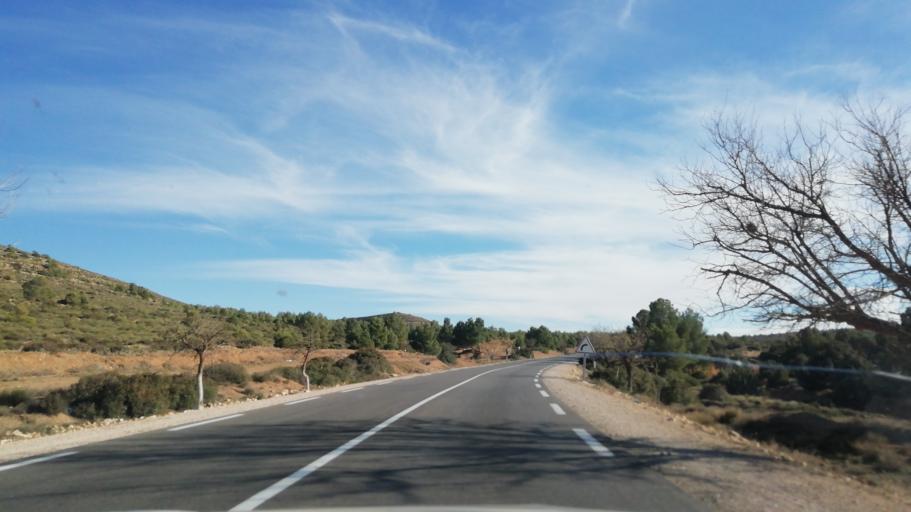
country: DZ
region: Tlemcen
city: Sebdou
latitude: 34.5947
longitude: -1.3204
